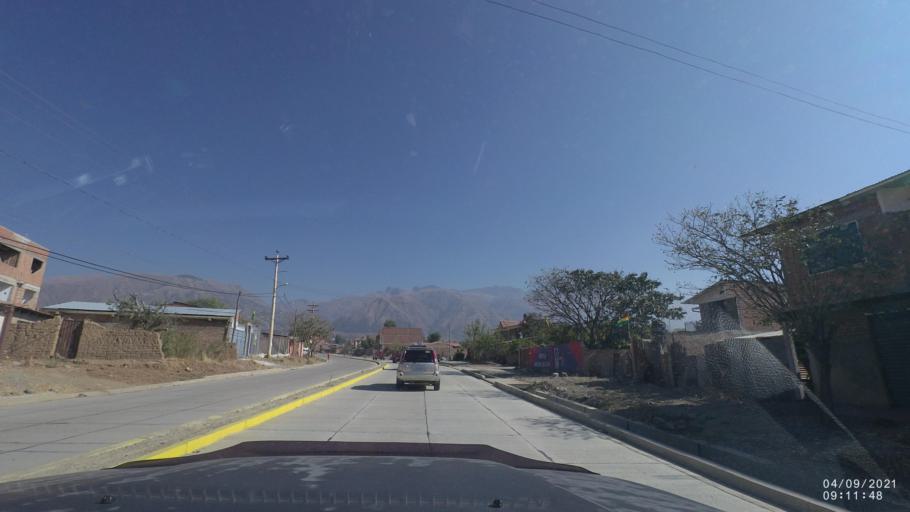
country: BO
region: Cochabamba
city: Sipe Sipe
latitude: -17.3876
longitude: -66.3364
